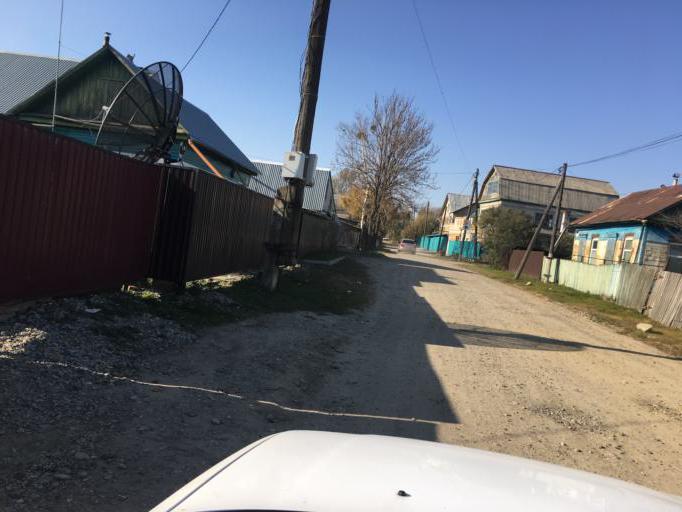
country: RU
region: Primorskiy
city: Dal'nerechensk
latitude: 45.9252
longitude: 133.7258
